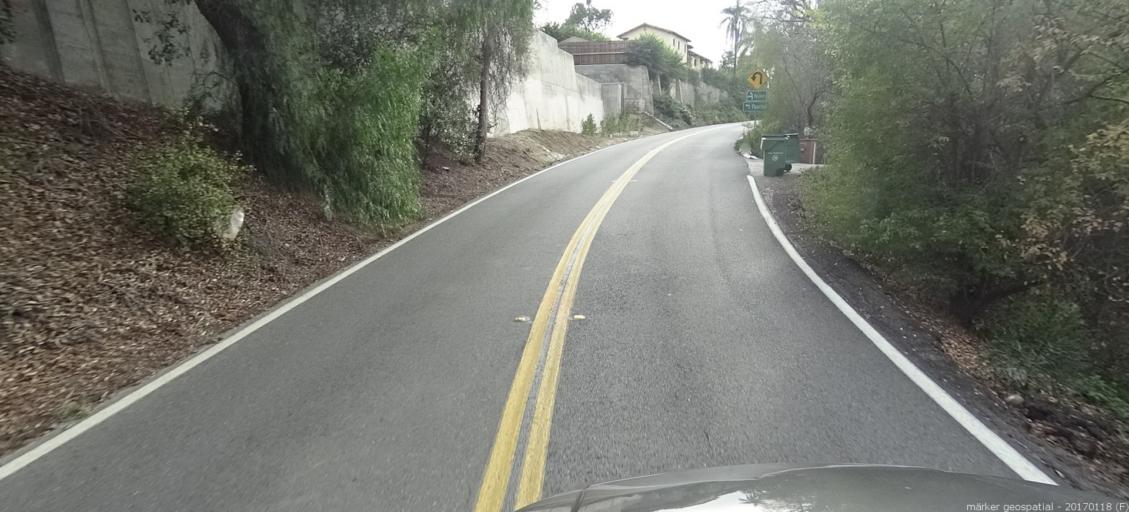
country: US
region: California
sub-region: Orange County
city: North Tustin
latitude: 33.7592
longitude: -117.7856
